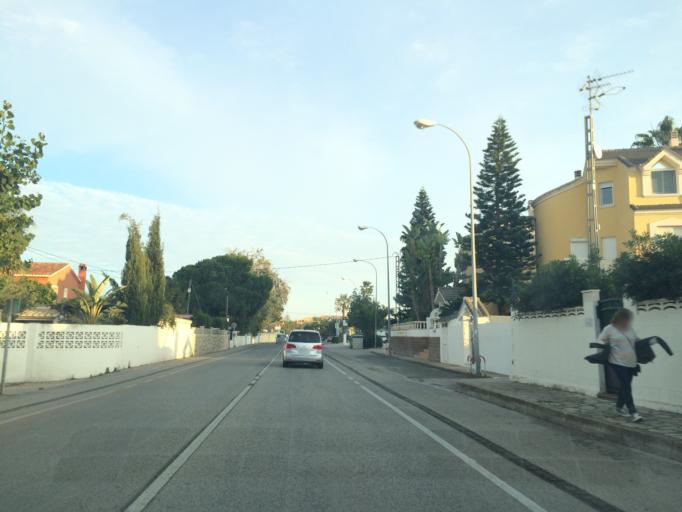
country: ES
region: Valencia
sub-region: Provincia de Alicante
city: Denia
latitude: 38.8545
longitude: 0.0835
